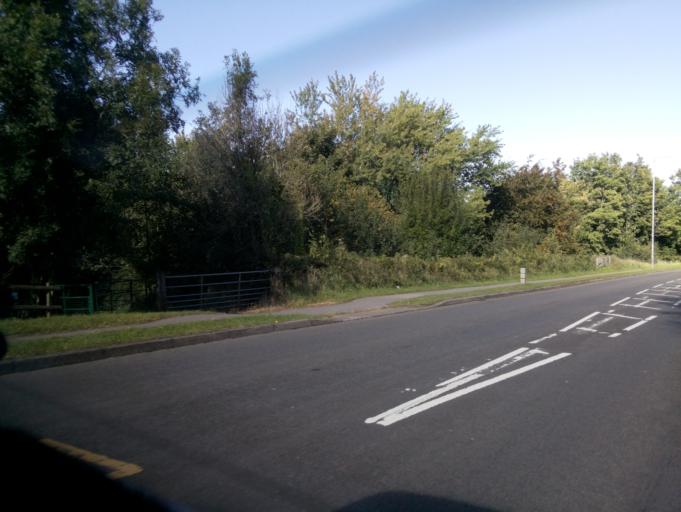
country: GB
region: Wales
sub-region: Torfaen County Borough
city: Cwmbran
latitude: 51.6350
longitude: -3.0514
